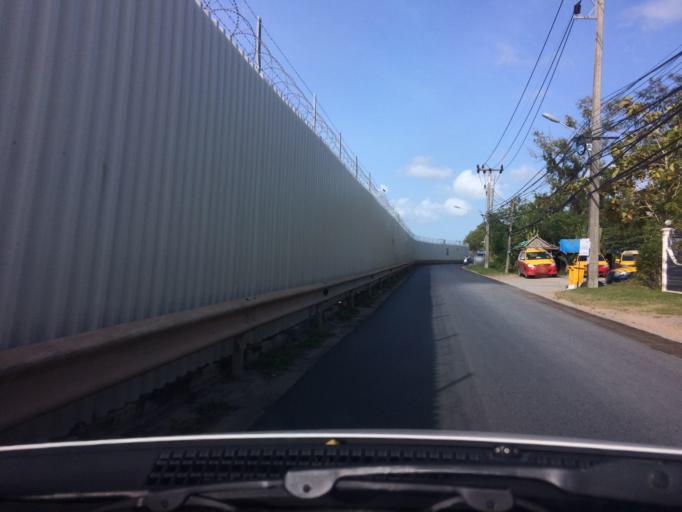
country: TH
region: Phuket
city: Thalang
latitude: 8.1109
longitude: 98.3112
